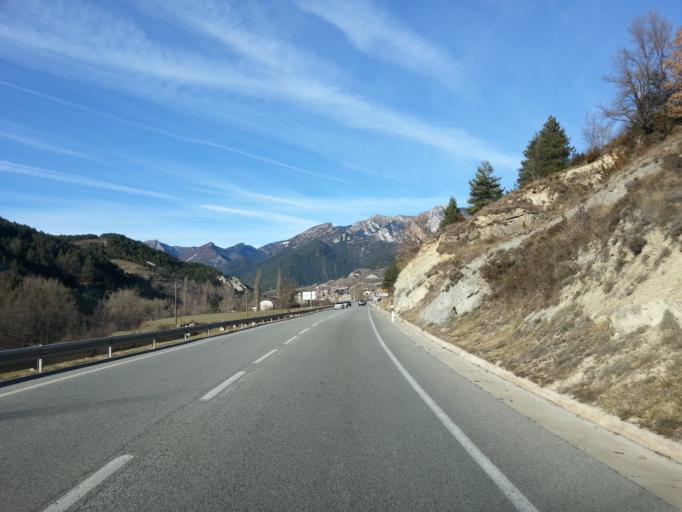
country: ES
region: Catalonia
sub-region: Provincia de Barcelona
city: Guardiola de Bergueda
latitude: 42.2426
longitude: 1.8724
